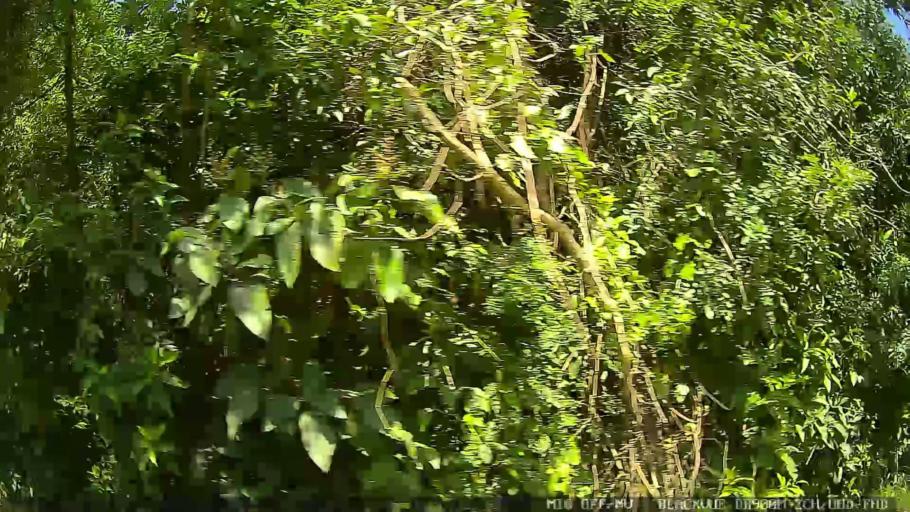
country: BR
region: Sao Paulo
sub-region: Guaruja
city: Guaruja
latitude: -24.0102
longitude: -46.2819
